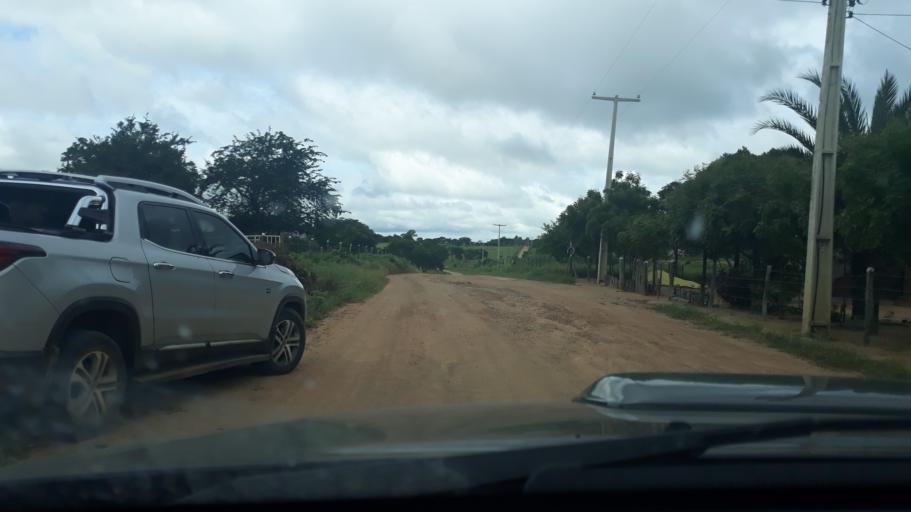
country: BR
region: Bahia
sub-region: Riacho De Santana
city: Riacho de Santana
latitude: -13.9054
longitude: -42.9026
